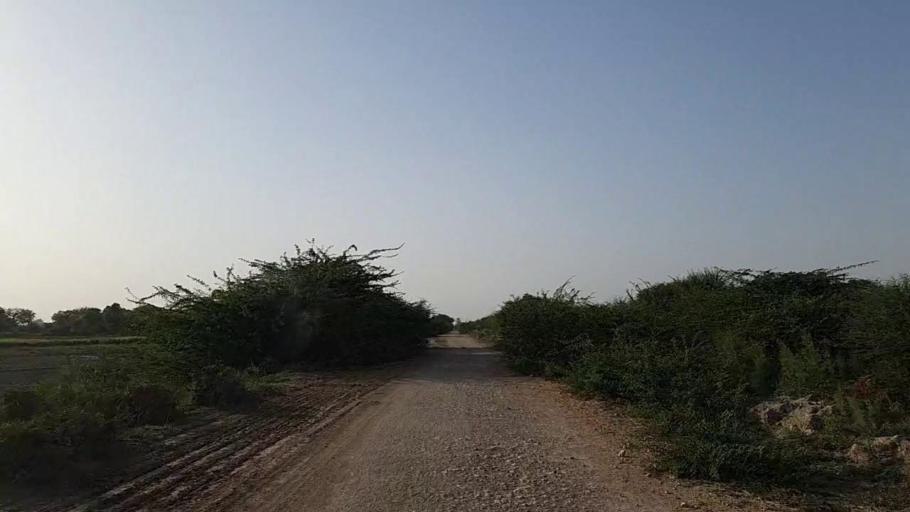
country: PK
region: Sindh
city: Jati
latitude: 24.3391
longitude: 68.1500
